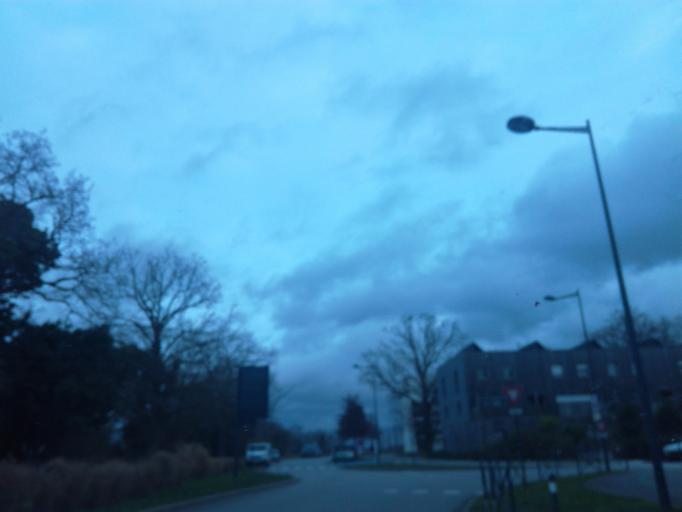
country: FR
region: Brittany
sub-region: Departement d'Ille-et-Vilaine
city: Chantepie
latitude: 48.0873
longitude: -1.6022
